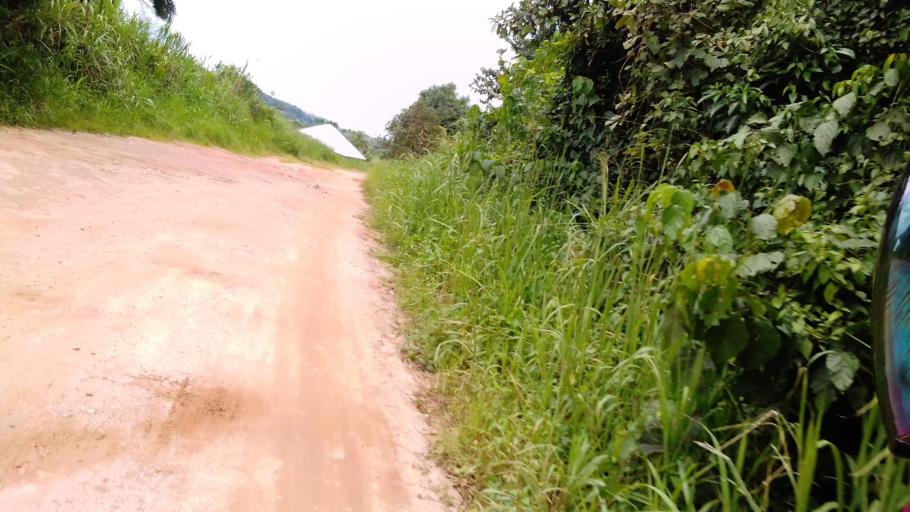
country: SL
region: Eastern Province
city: Koyima
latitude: 8.6929
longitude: -11.0102
